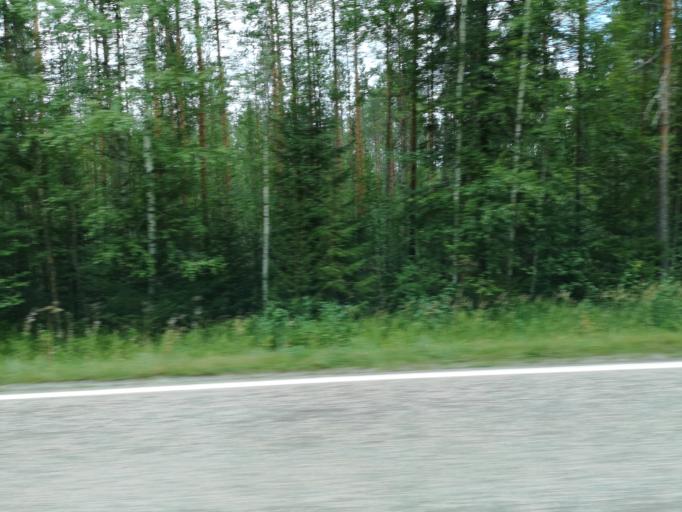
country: FI
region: Central Finland
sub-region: Jyvaeskylae
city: Hankasalmi
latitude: 62.3577
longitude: 26.5009
